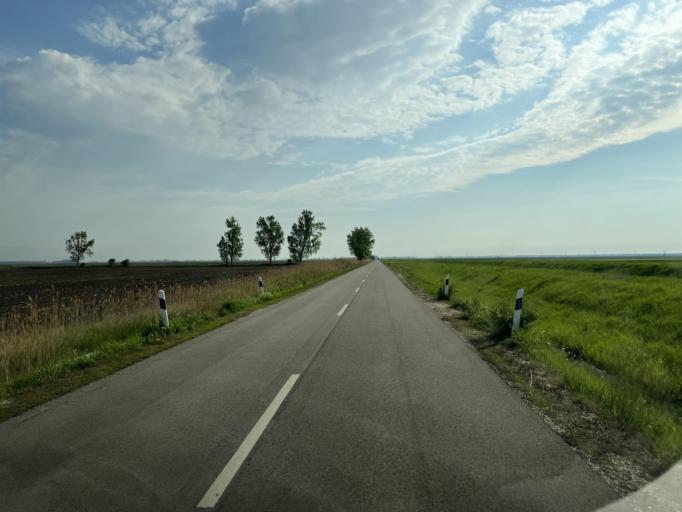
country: HU
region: Pest
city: Jaszkarajeno
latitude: 47.1022
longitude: 20.0315
